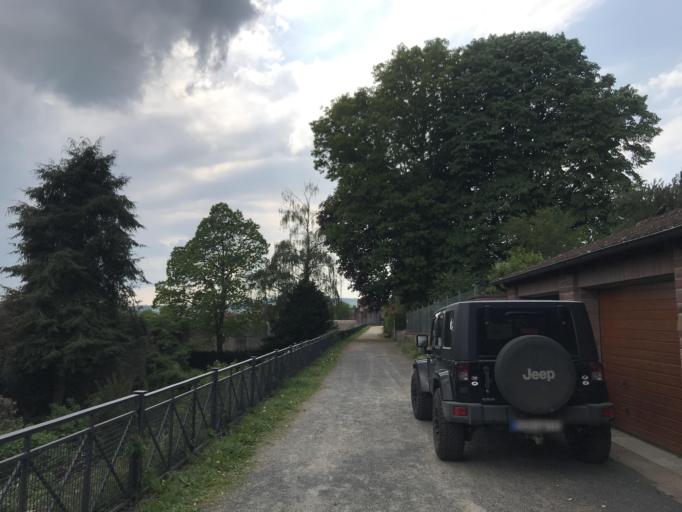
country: DE
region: Hesse
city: Budingen
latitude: 50.2944
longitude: 9.1167
